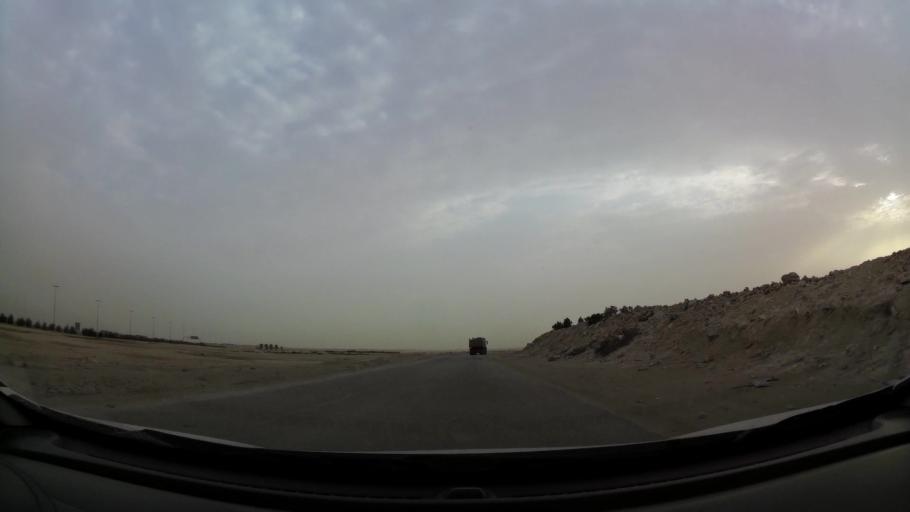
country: BH
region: Northern
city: Ar Rifa'
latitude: 26.0392
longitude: 50.6066
